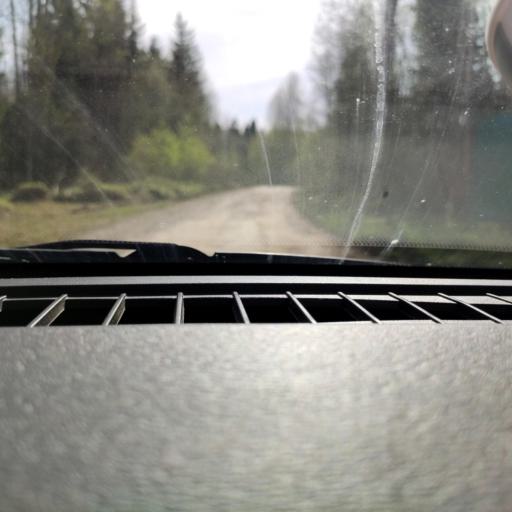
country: RU
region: Perm
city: Kondratovo
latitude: 58.2593
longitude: 56.1085
